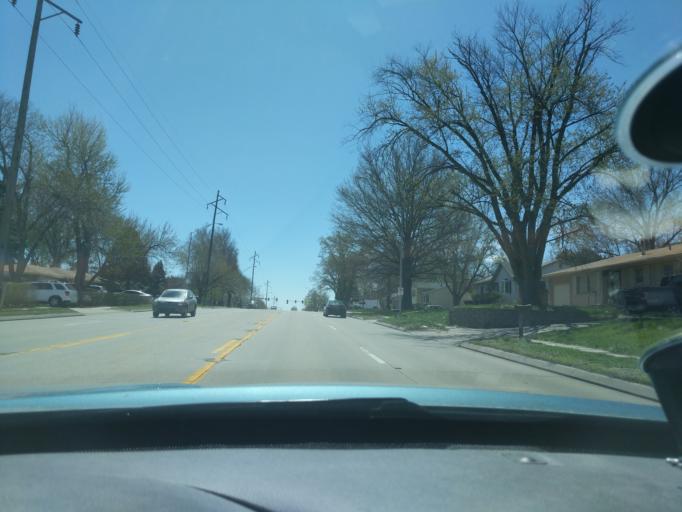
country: US
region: Nebraska
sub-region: Douglas County
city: Ralston
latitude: 41.2286
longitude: -96.1008
